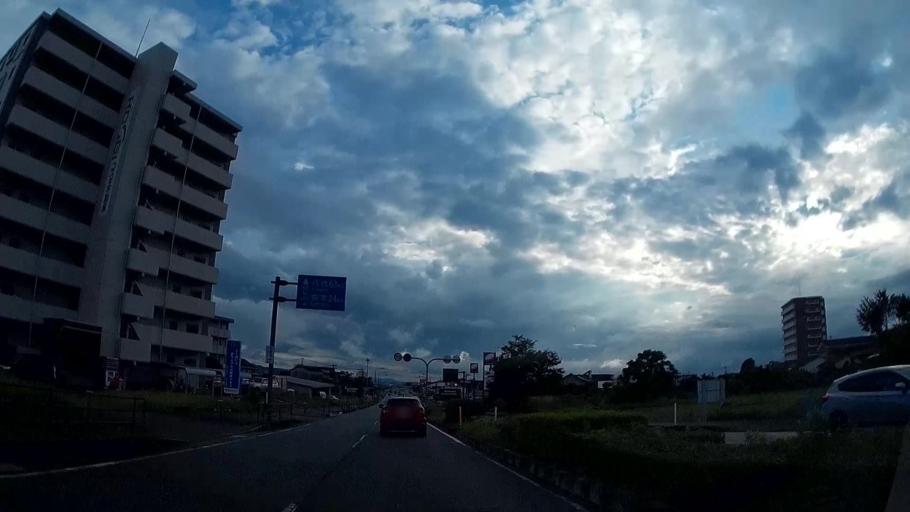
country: JP
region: Kumamoto
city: Ozu
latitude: 32.8794
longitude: 130.8882
